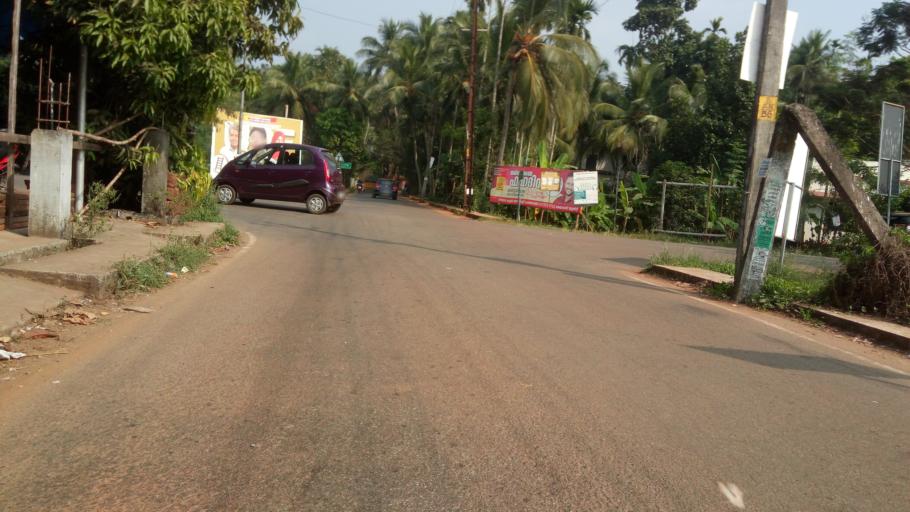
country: IN
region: Kerala
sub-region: Malappuram
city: Malappuram
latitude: 10.9941
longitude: 76.0139
